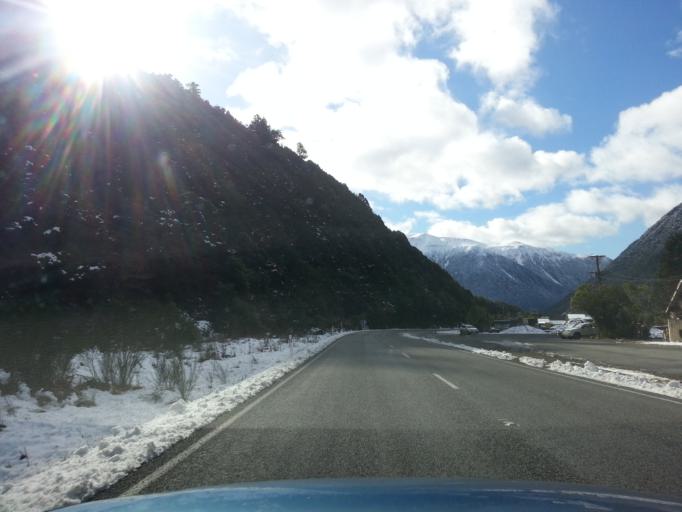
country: NZ
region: West Coast
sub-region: Grey District
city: Greymouth
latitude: -42.8440
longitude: 171.5599
